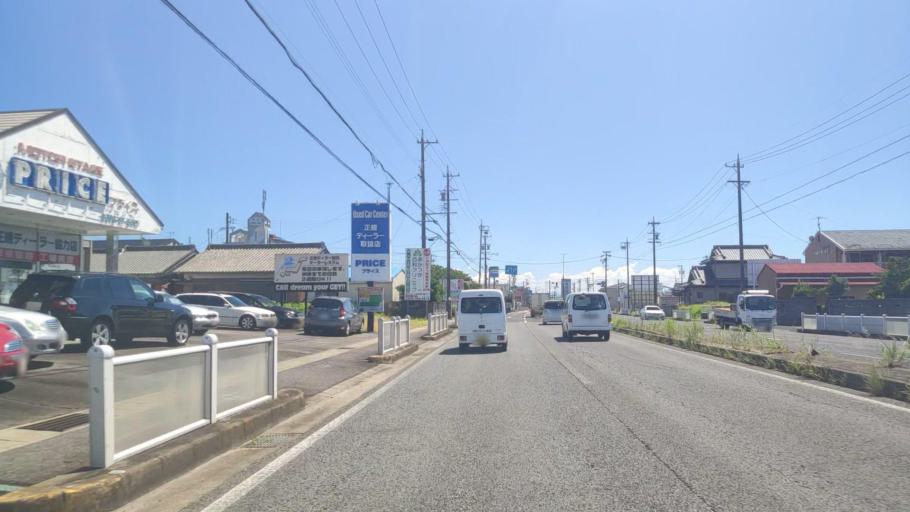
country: JP
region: Mie
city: Kawage
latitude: 34.8143
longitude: 136.5696
